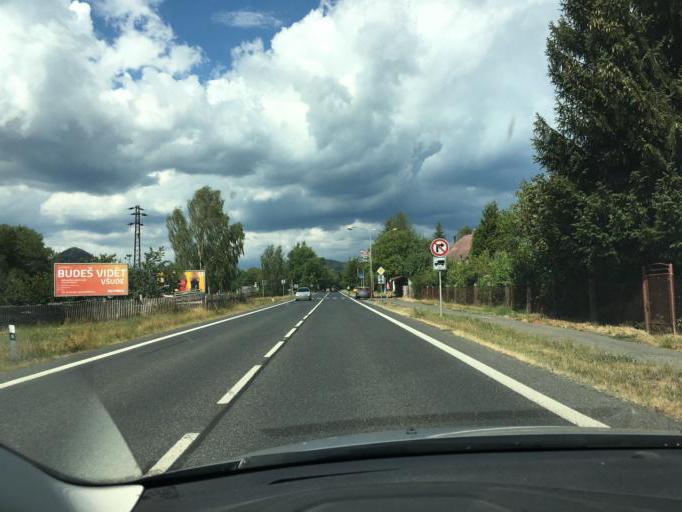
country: CZ
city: Cvikov
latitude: 50.7766
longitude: 14.6273
